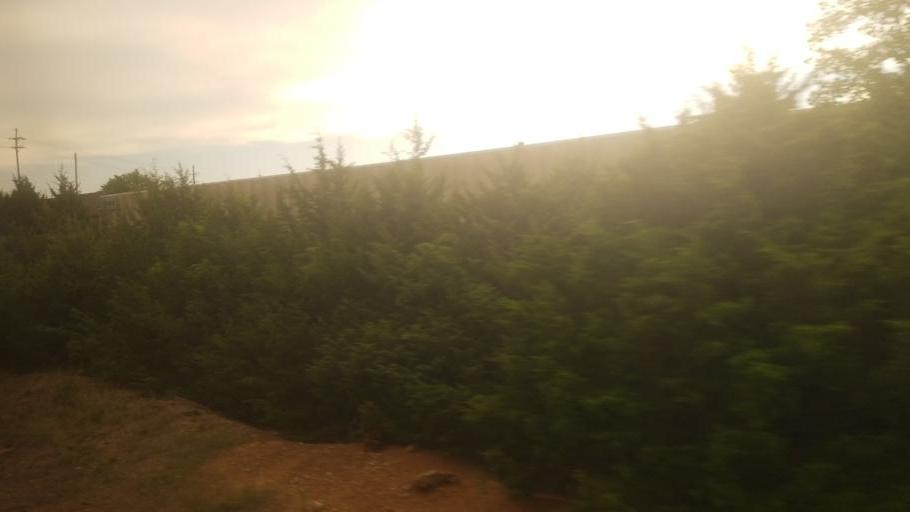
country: US
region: Kansas
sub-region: Shawnee County
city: Topeka
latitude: 38.9996
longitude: -95.6837
